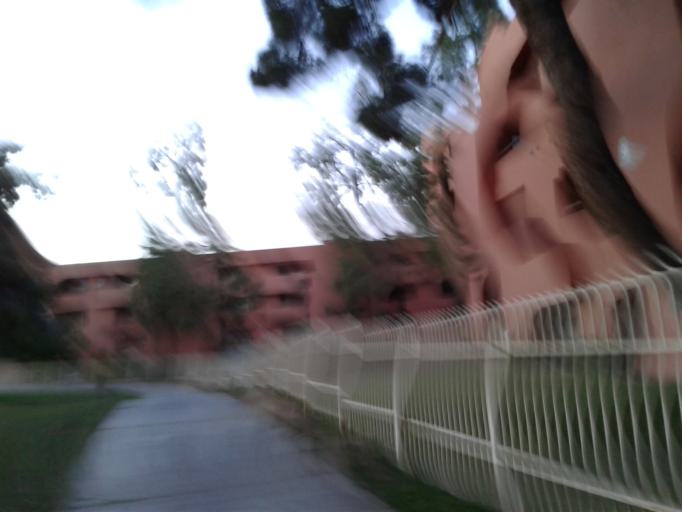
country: US
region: Arizona
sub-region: Maricopa County
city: Paradise Valley
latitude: 33.5973
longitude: -111.9900
